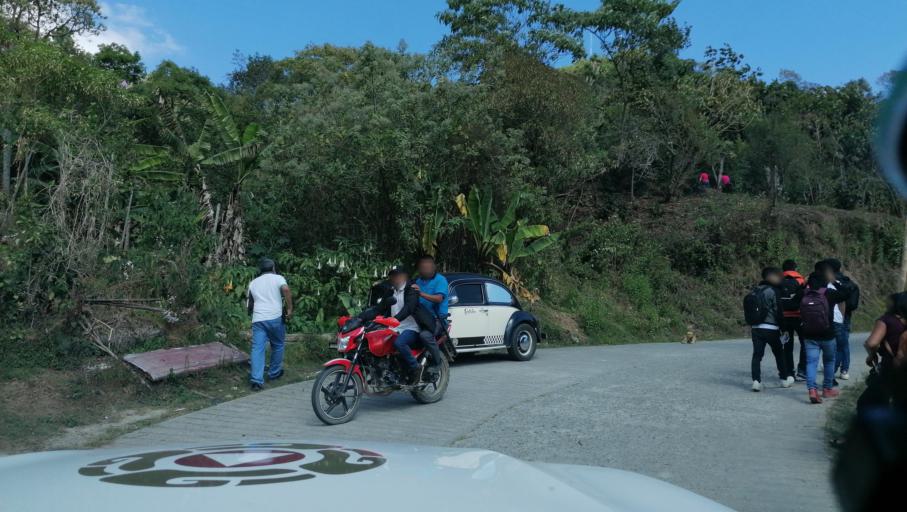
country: GT
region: San Marcos
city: Tacana
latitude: 15.2018
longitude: -92.2041
